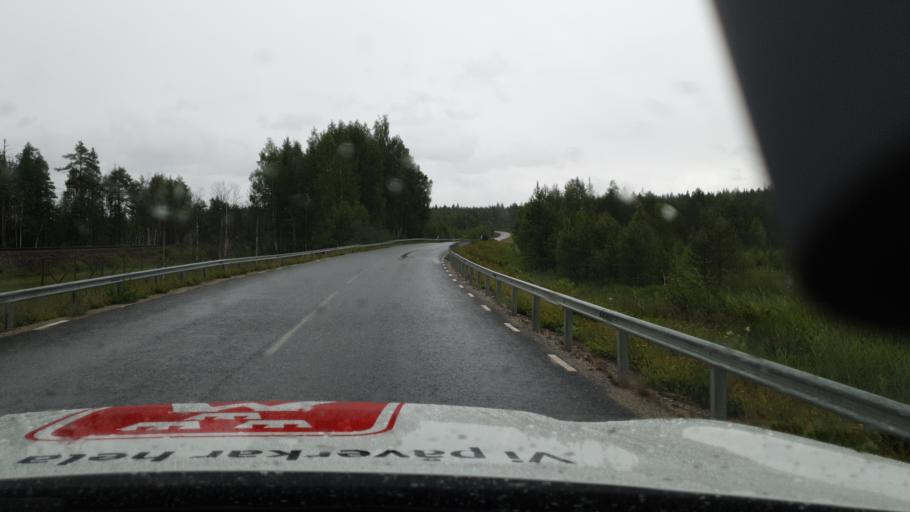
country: SE
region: Vaesterbotten
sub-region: Vindelns Kommun
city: Vindeln
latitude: 64.4543
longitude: 19.7484
